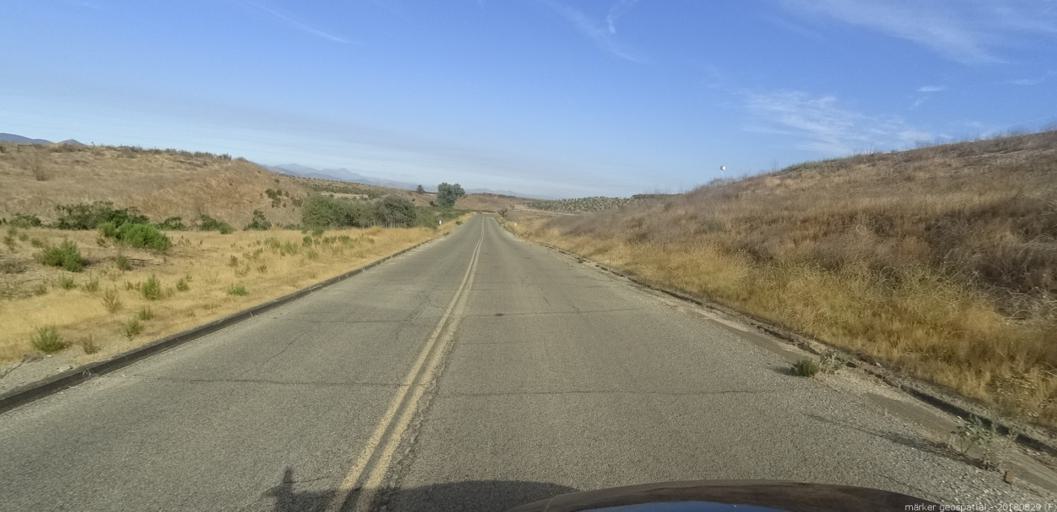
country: US
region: California
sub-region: Monterey County
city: King City
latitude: 36.0793
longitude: -120.9992
